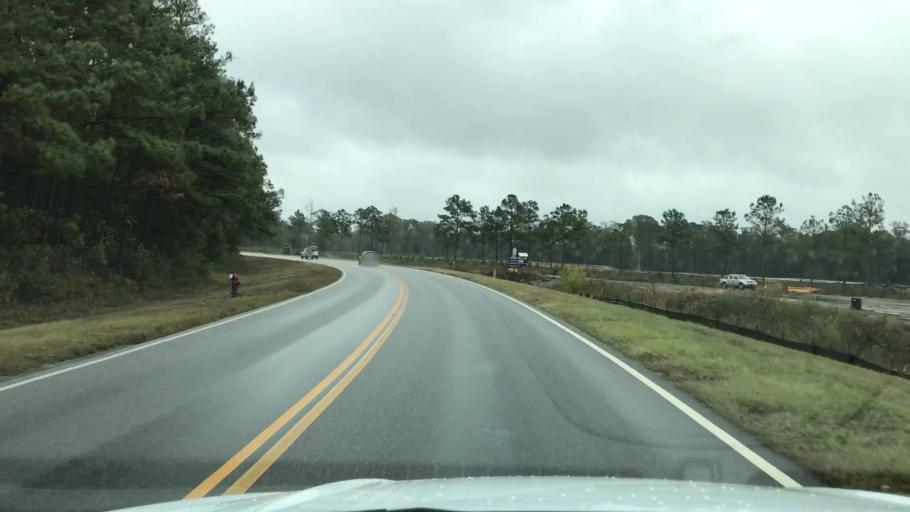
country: US
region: South Carolina
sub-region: Horry County
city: Myrtle Beach
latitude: 33.7543
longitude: -78.8807
